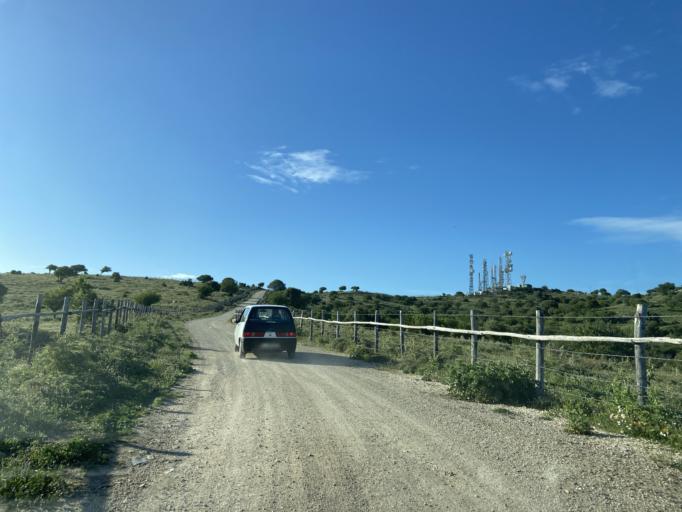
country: IT
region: Latium
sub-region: Citta metropolitana di Roma Capitale
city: Santa Marinella
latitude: 42.0853
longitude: 11.8527
